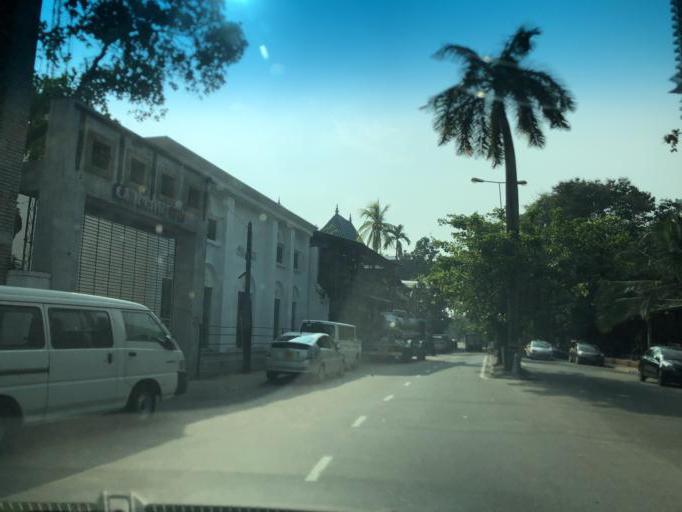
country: LK
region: Western
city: Colombo
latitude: 6.9169
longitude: 79.8573
